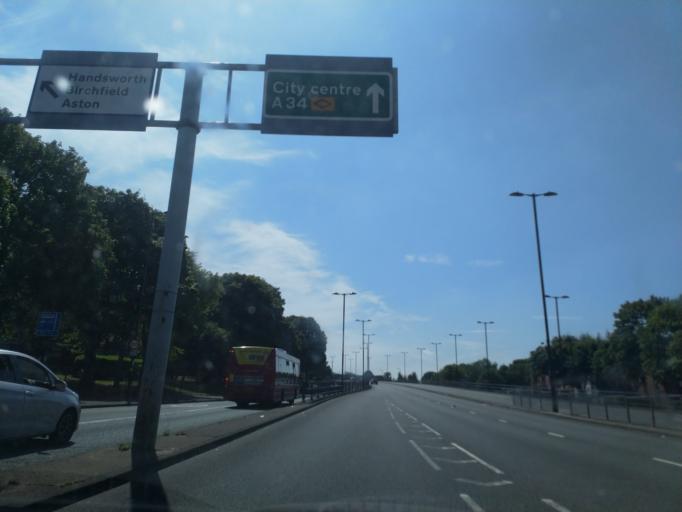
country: GB
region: England
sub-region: City and Borough of Birmingham
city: Hockley
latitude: 52.5111
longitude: -1.9025
